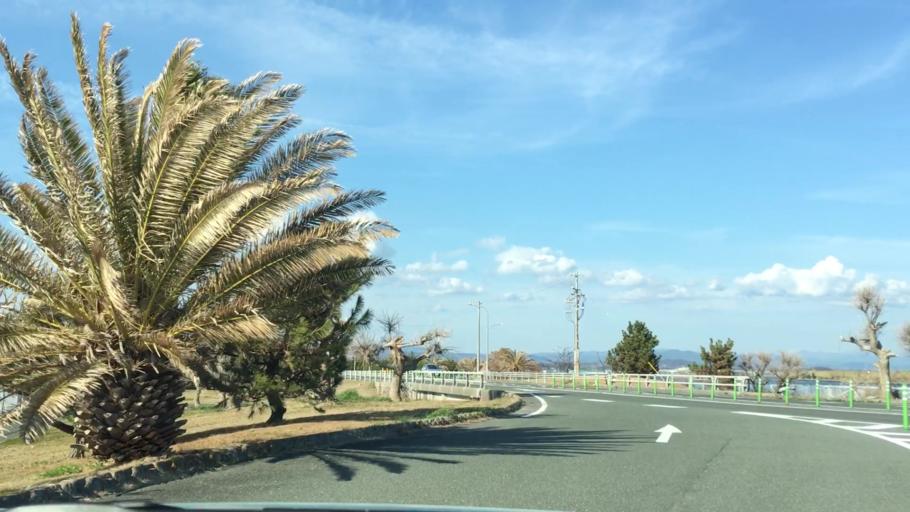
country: JP
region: Shizuoka
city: Kosai-shi
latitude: 34.7046
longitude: 137.6101
